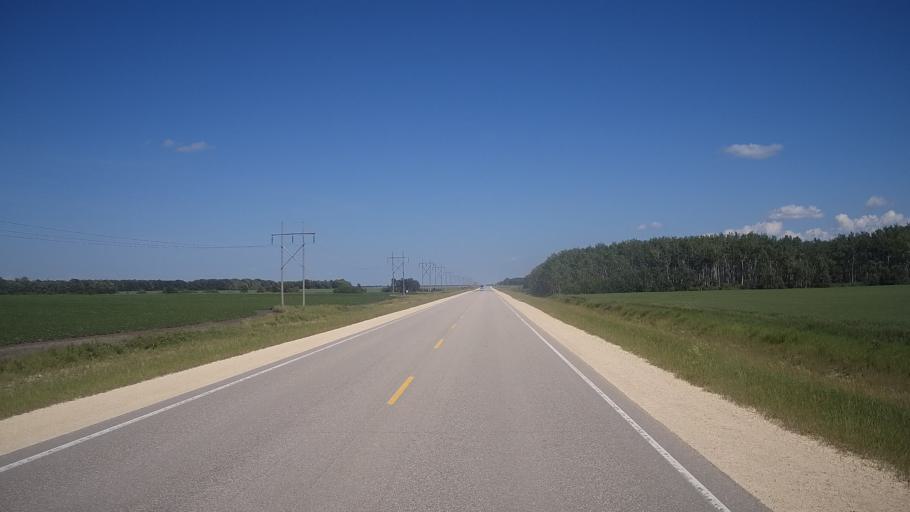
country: CA
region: Manitoba
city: Stonewall
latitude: 50.1227
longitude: -97.4544
